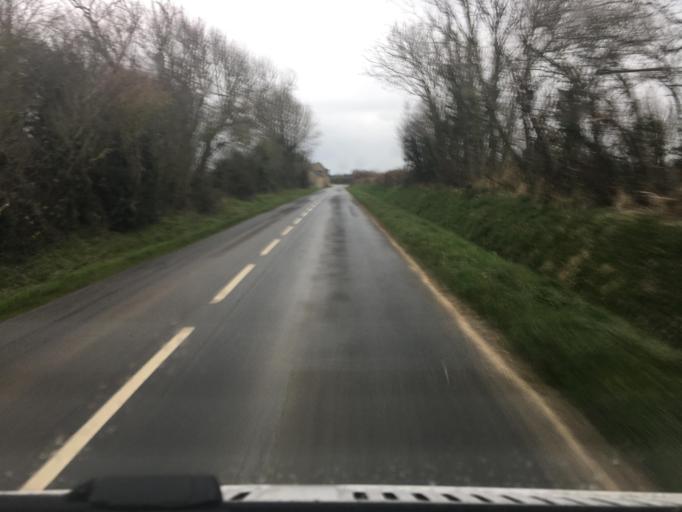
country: FR
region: Lower Normandy
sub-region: Departement du Calvados
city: Grandcamp-Maisy
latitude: 49.3820
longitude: -0.9218
